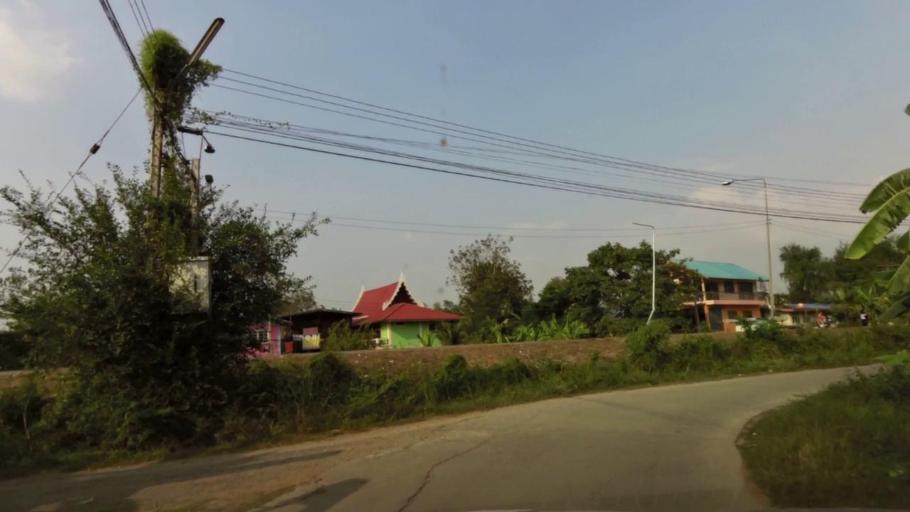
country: TH
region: Phra Nakhon Si Ayutthaya
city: Phra Nakhon Si Ayutthaya
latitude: 14.3342
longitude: 100.5647
